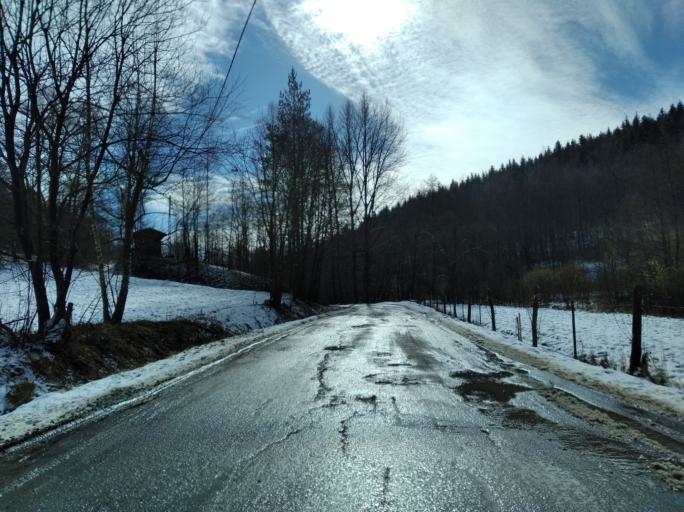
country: PL
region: Subcarpathian Voivodeship
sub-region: Powiat brzozowski
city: Jablonica Polska
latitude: 49.7382
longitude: 21.8869
